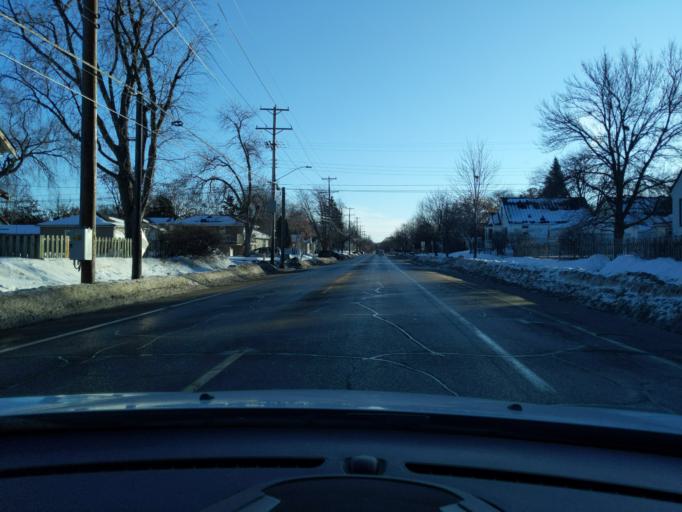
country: US
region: Minnesota
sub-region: Hennepin County
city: Minneapolis
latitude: 44.9269
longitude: -93.2410
